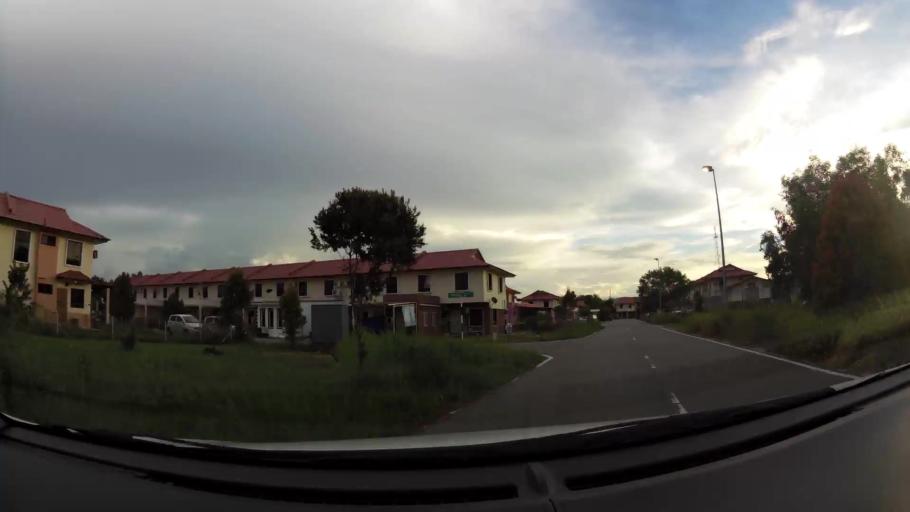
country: BN
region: Brunei and Muara
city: Bandar Seri Begawan
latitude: 4.9933
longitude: 114.9904
